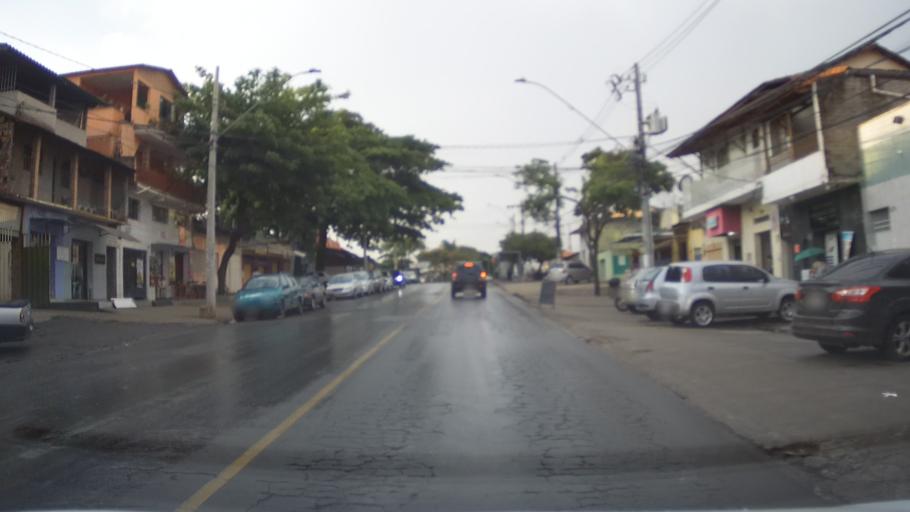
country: BR
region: Minas Gerais
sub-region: Belo Horizonte
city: Belo Horizonte
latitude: -19.9666
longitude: -43.9816
